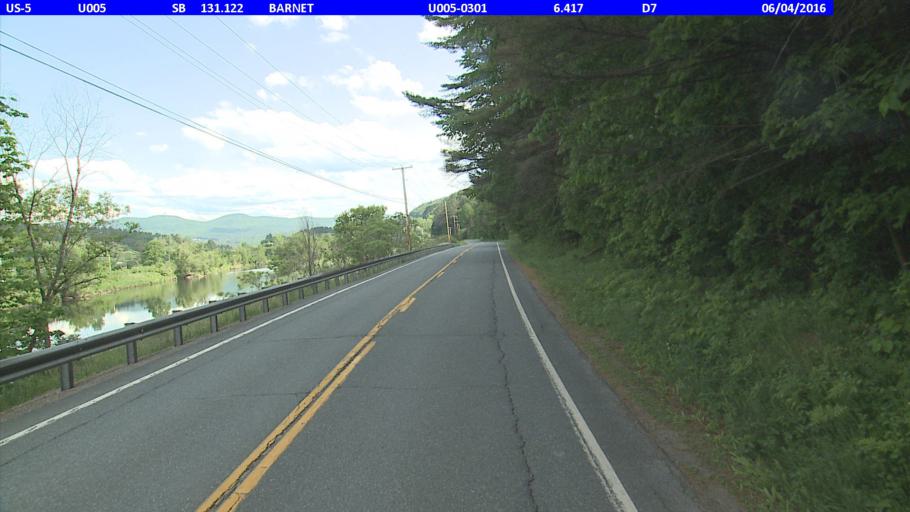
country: US
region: Vermont
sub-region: Caledonia County
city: Saint Johnsbury
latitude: 44.3366
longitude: -72.0425
